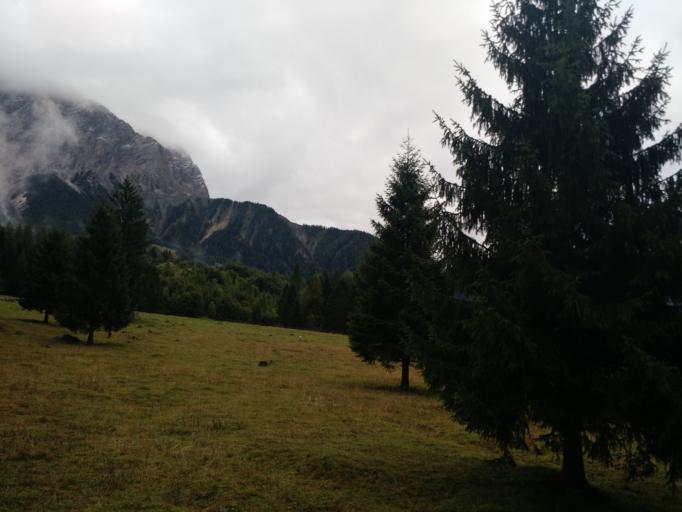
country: AT
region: Tyrol
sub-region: Politischer Bezirk Reutte
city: Ehrwald
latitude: 47.4163
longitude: 10.9169
